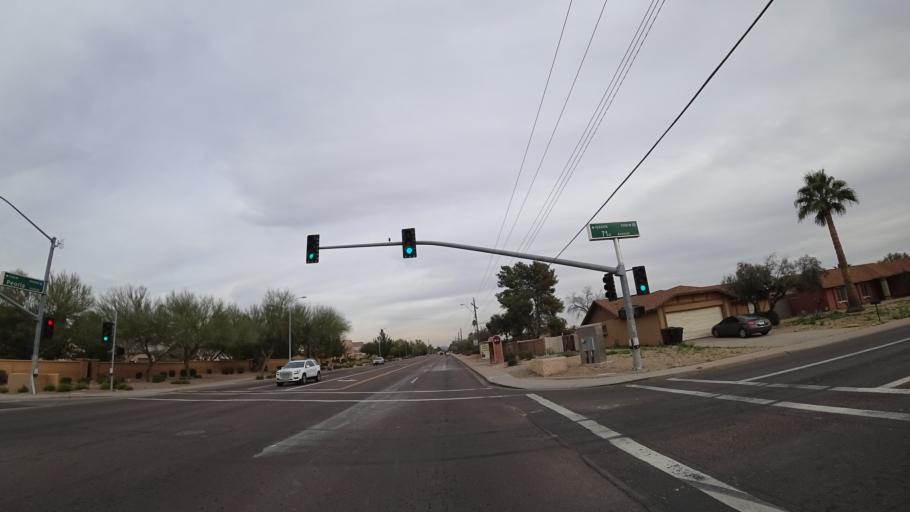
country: US
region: Arizona
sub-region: Maricopa County
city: Peoria
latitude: 33.5815
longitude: -112.2116
